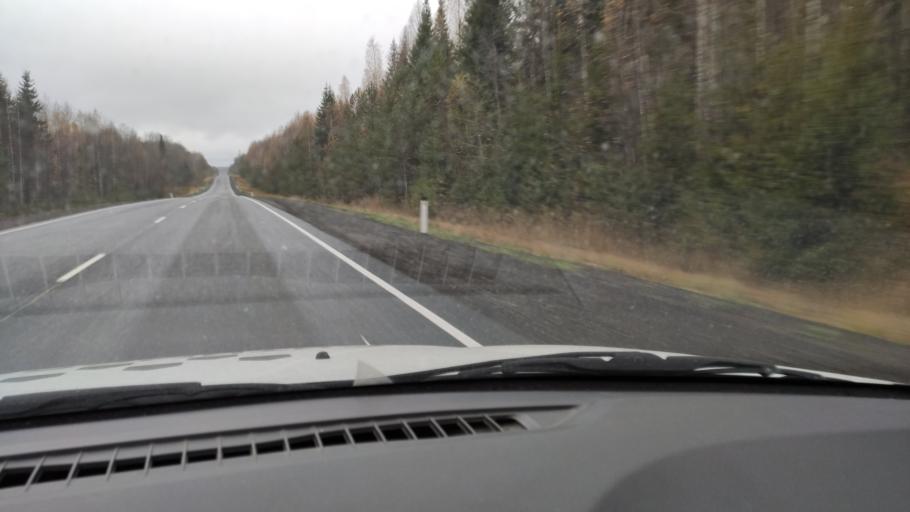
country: RU
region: Kirov
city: Chernaya Kholunitsa
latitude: 58.8833
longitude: 51.4169
